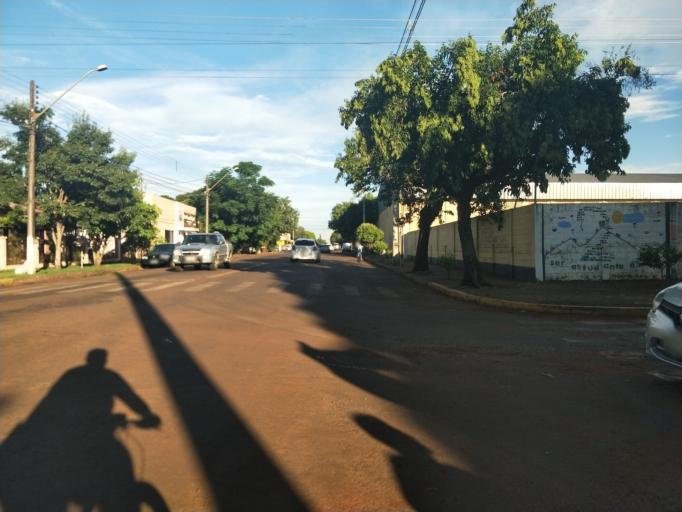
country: BR
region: Parana
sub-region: Marechal Candido Rondon
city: Marechal Candido Rondon
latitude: -24.5555
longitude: -54.0576
